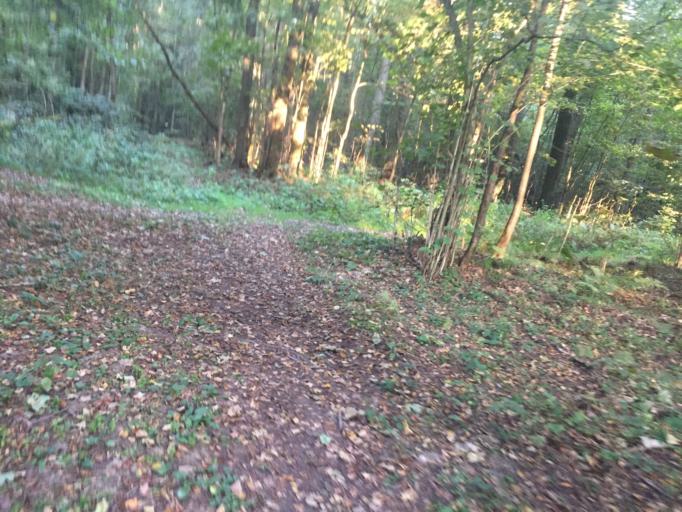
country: RU
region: Moscow
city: Gol'yanovo
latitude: 55.8498
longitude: 37.8124
